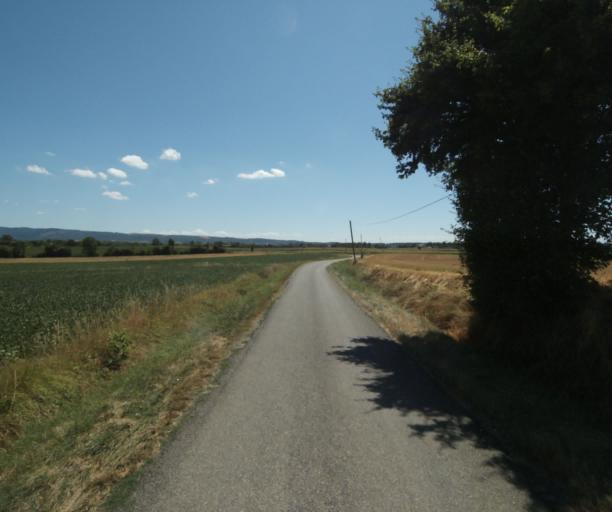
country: FR
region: Midi-Pyrenees
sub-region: Departement de la Haute-Garonne
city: Saint-Felix-Lauragais
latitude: 43.4580
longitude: 1.9289
